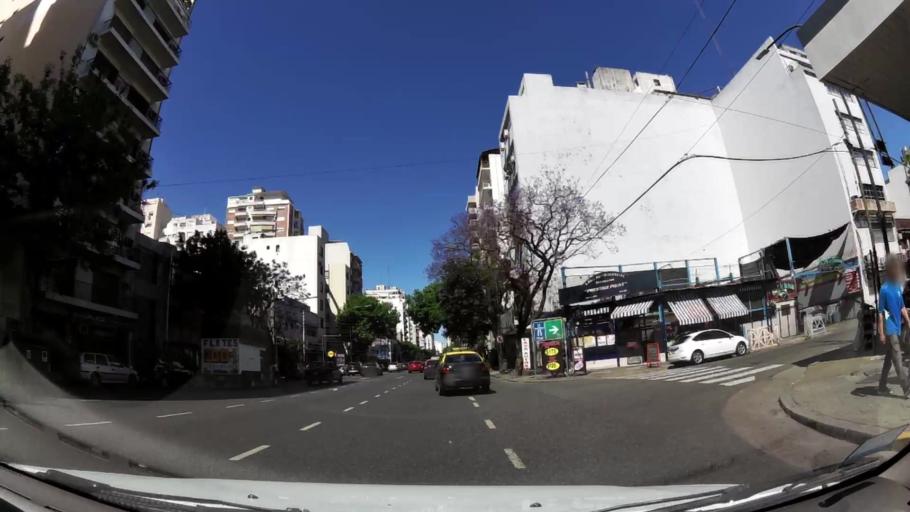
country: AR
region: Buenos Aires F.D.
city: Buenos Aires
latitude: -34.6240
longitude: -58.4035
